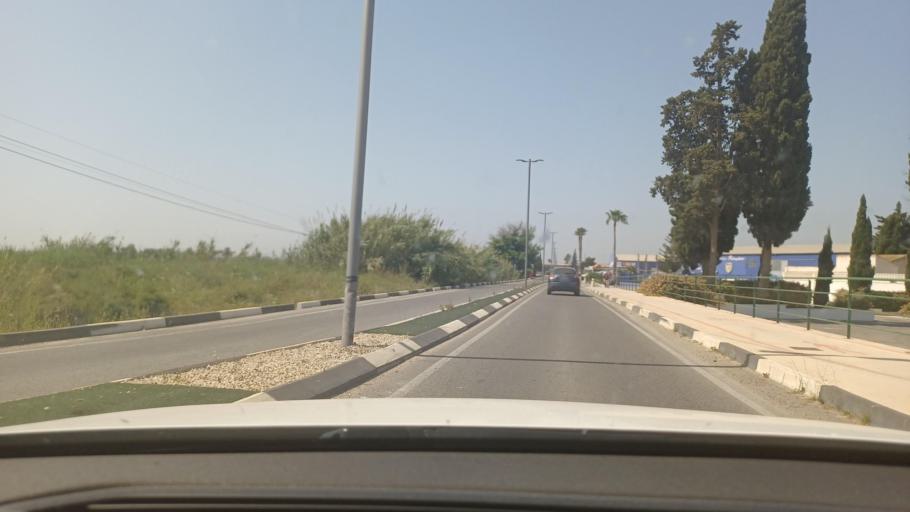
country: ES
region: Valencia
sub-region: Provincia de Alicante
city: Dolores
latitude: 38.1298
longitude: -0.7771
